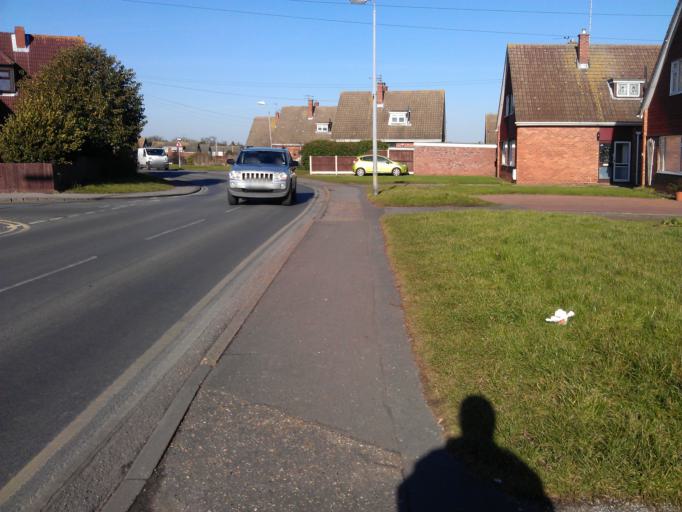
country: GB
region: England
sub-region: Essex
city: Clacton-on-Sea
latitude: 51.8075
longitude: 1.1551
